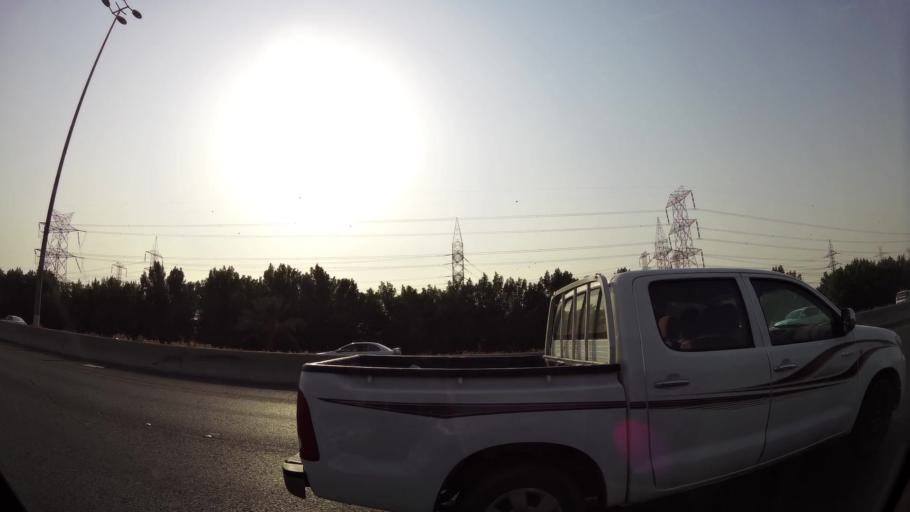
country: KW
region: Mubarak al Kabir
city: Sabah as Salim
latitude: 29.2212
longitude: 48.0555
